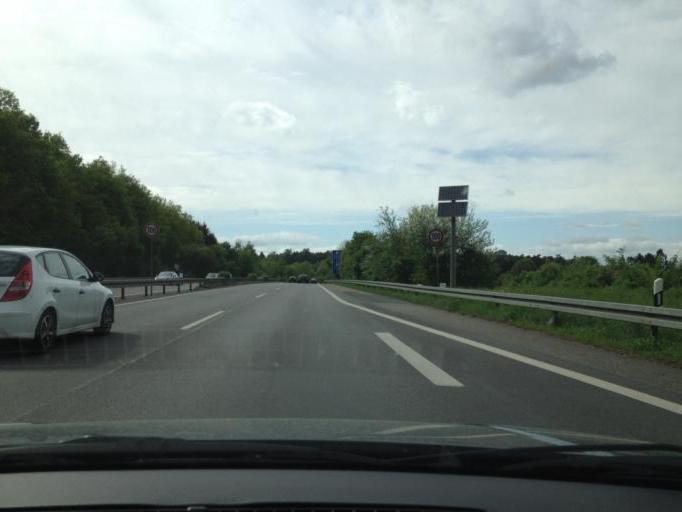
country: DE
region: Saarland
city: Kirkel
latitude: 49.3115
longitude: 7.2489
